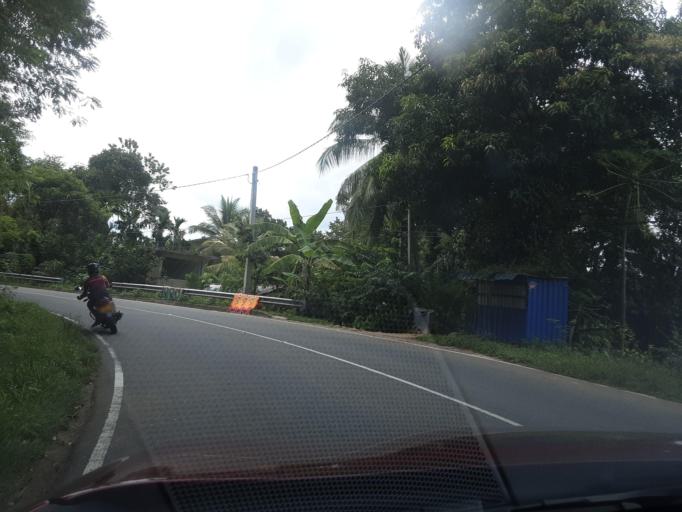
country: LK
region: Uva
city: Monaragala
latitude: 6.8994
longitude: 81.2513
